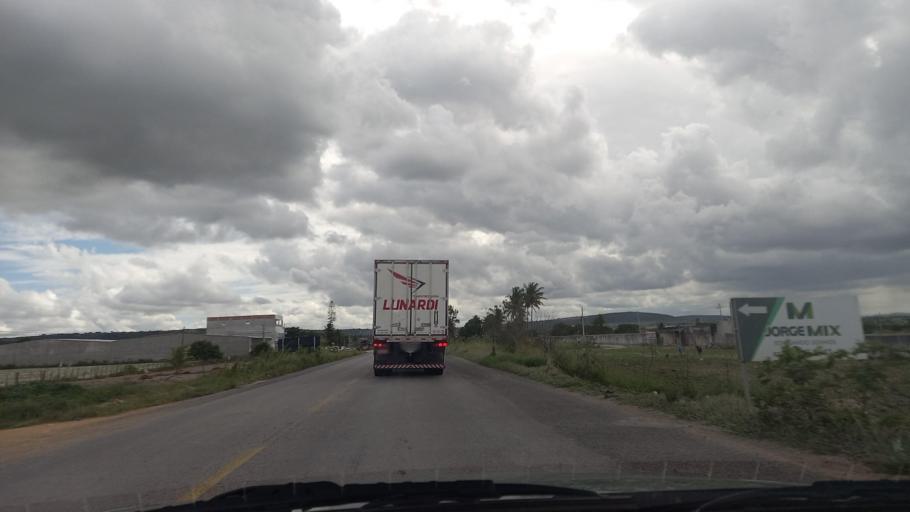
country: BR
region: Pernambuco
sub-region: Lajedo
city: Lajedo
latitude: -8.6630
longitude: -36.3510
